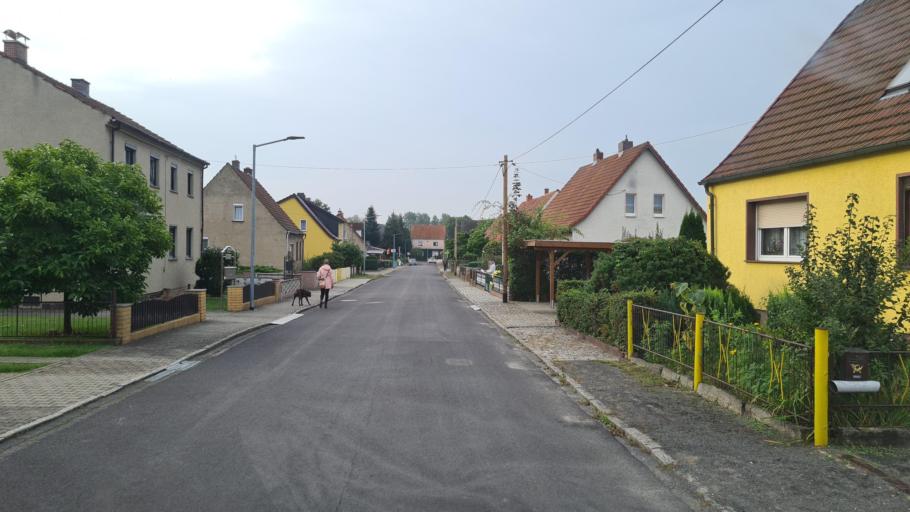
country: DE
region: Brandenburg
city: Lauchhammer
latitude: 51.4941
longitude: 13.7722
